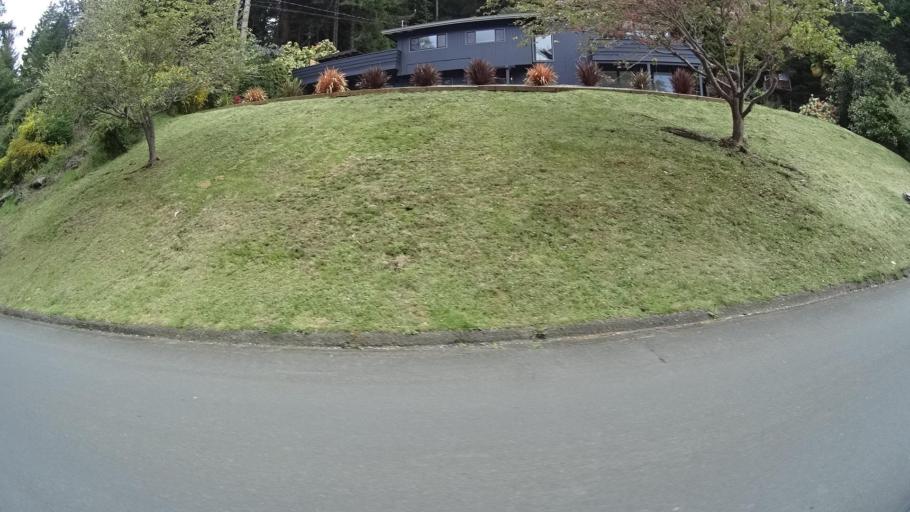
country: US
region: California
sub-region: Humboldt County
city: Bayside
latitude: 40.8519
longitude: -124.0527
